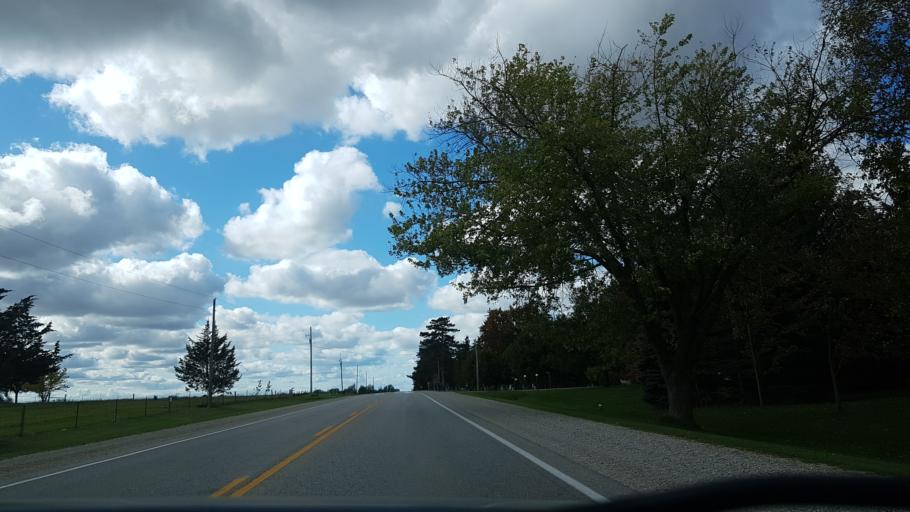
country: CA
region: Ontario
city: South Huron
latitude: 43.3599
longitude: -81.5012
